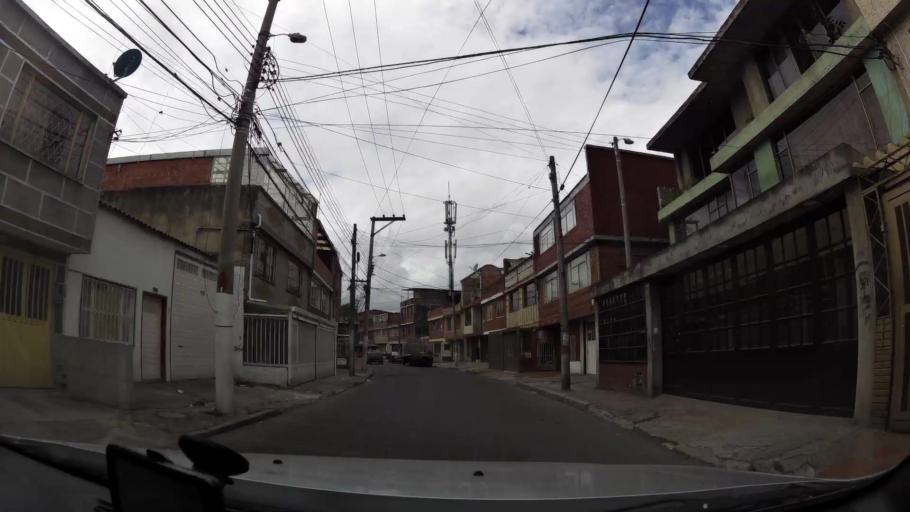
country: CO
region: Bogota D.C.
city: Bogota
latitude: 4.6175
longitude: -74.1120
